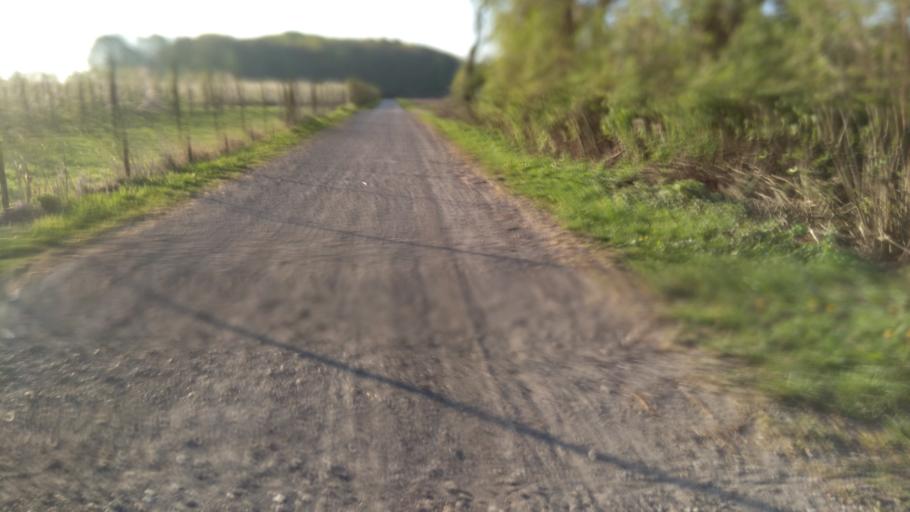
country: DE
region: Lower Saxony
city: Bliedersdorf
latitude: 53.4737
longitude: 9.5812
